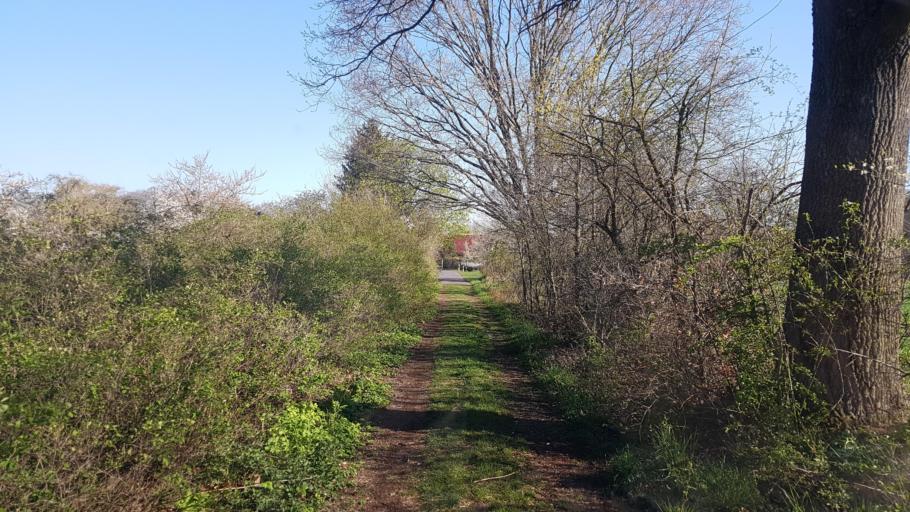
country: DE
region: Brandenburg
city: Bronkow
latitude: 51.6659
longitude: 13.9164
